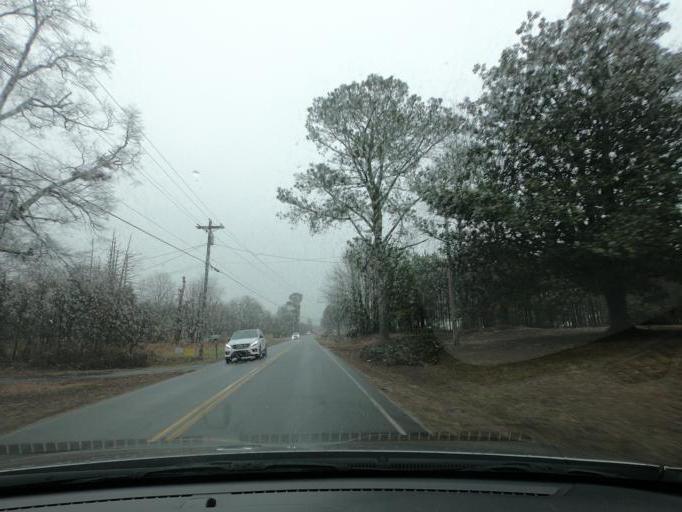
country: US
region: Georgia
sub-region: Fulton County
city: Milton
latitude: 34.1436
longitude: -84.2560
